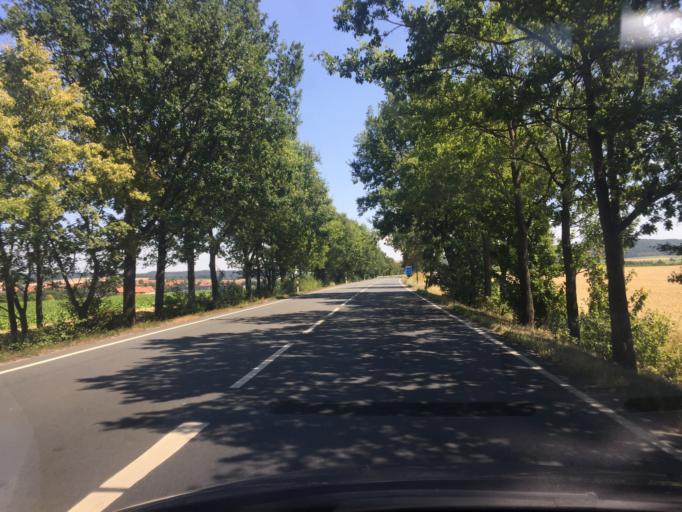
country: DE
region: Lower Saxony
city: Bockenem
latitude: 52.0007
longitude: 10.1472
